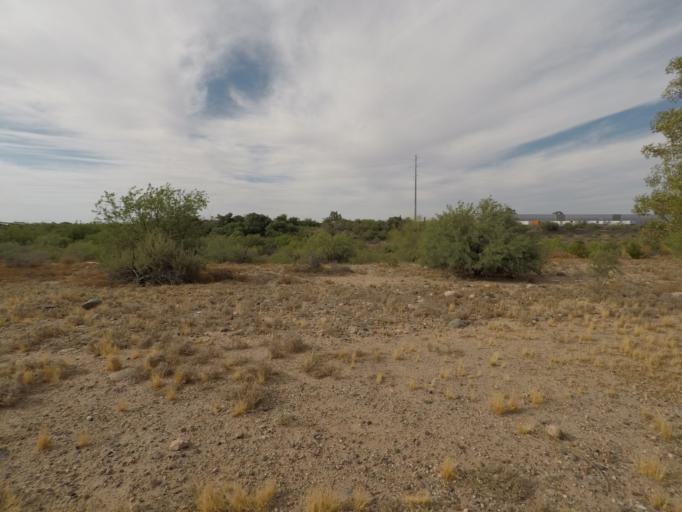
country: US
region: Arizona
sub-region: Maricopa County
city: Phoenix
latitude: 33.4201
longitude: -112.0698
